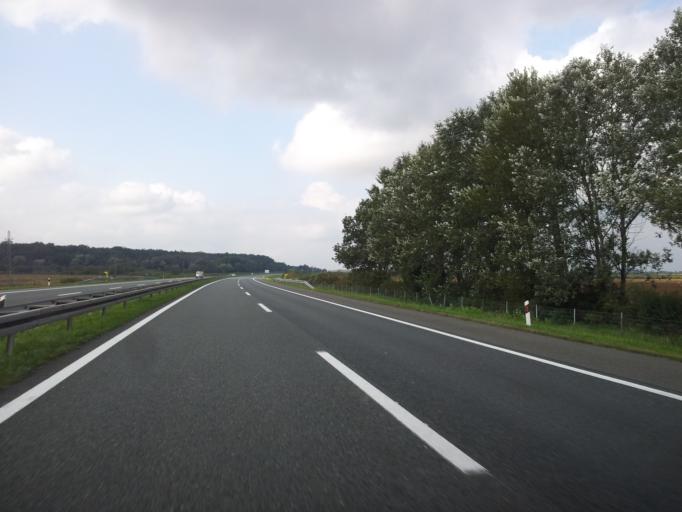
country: HR
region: Brodsko-Posavska
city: Okucani
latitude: 45.2293
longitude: 17.2420
